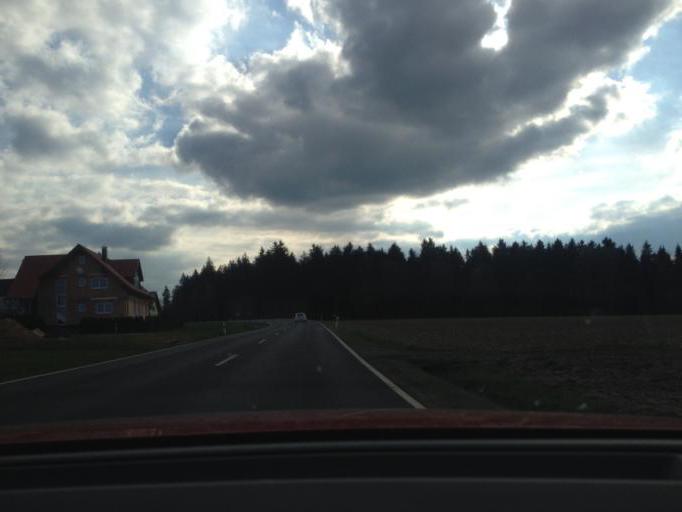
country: DE
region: Bavaria
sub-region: Upper Palatinate
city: Pullenreuth
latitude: 49.9514
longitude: 12.0266
